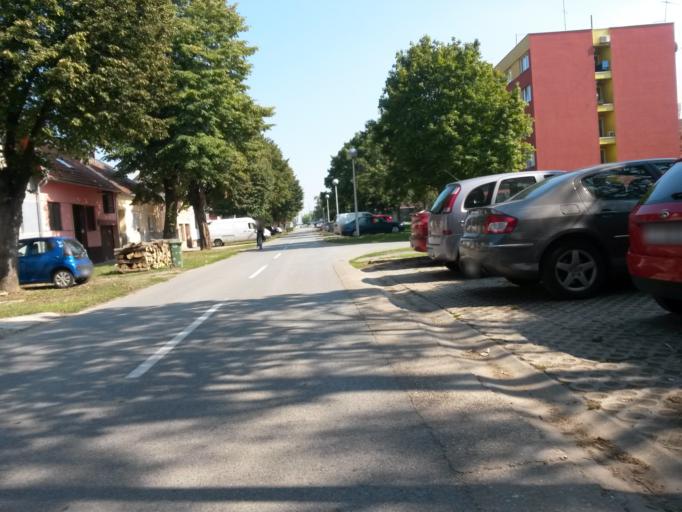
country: HR
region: Osjecko-Baranjska
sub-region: Grad Osijek
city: Osijek
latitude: 45.5467
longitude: 18.6763
